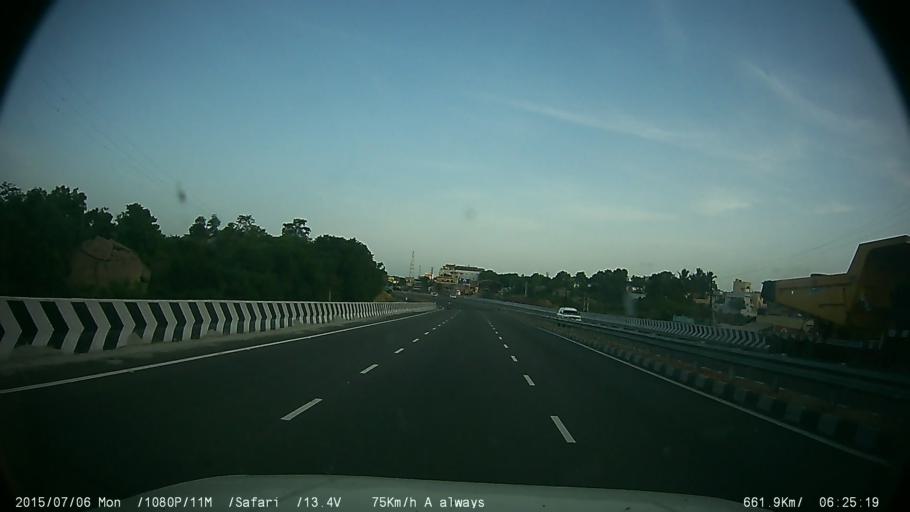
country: IN
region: Tamil Nadu
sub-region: Krishnagiri
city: Kelamangalam
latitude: 12.6608
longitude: 78.0163
